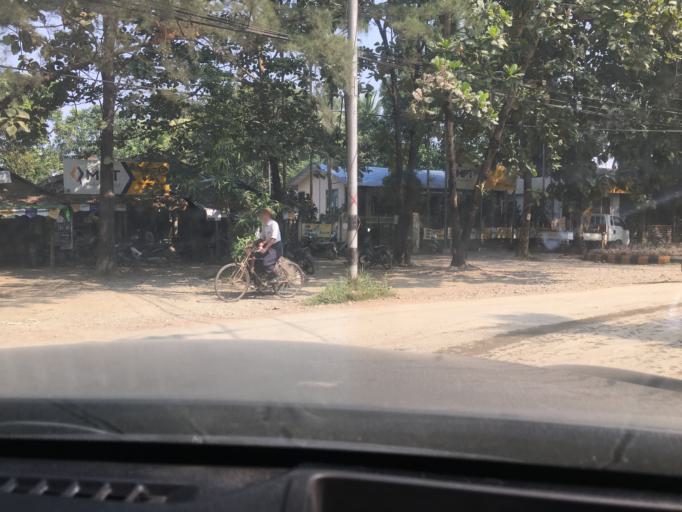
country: MM
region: Bago
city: Pyay
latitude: 18.4706
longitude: 94.3649
